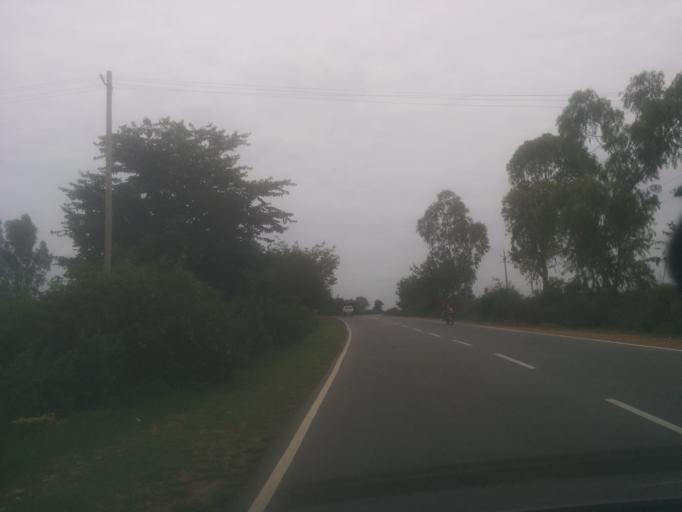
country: IN
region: Karnataka
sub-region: Hassan
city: Belur
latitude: 13.1630
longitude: 75.8973
